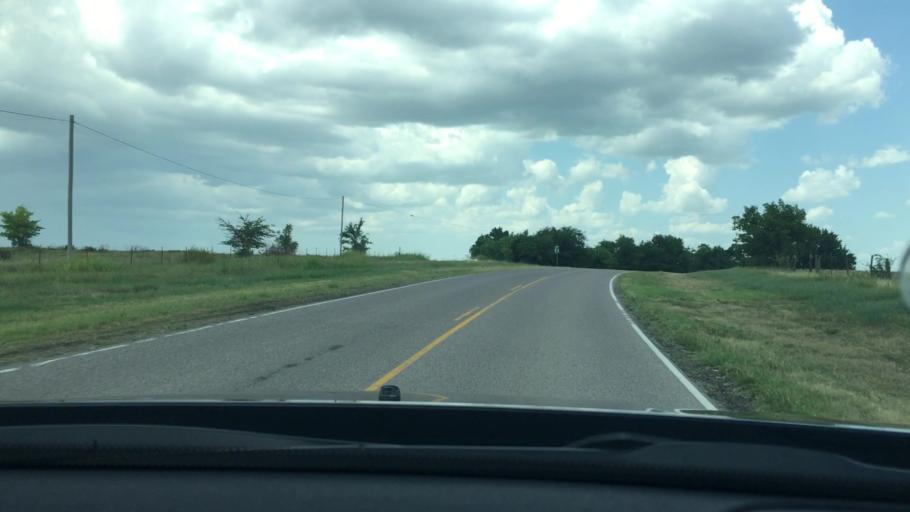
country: US
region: Oklahoma
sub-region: Johnston County
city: Tishomingo
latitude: 34.4707
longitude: -96.6359
